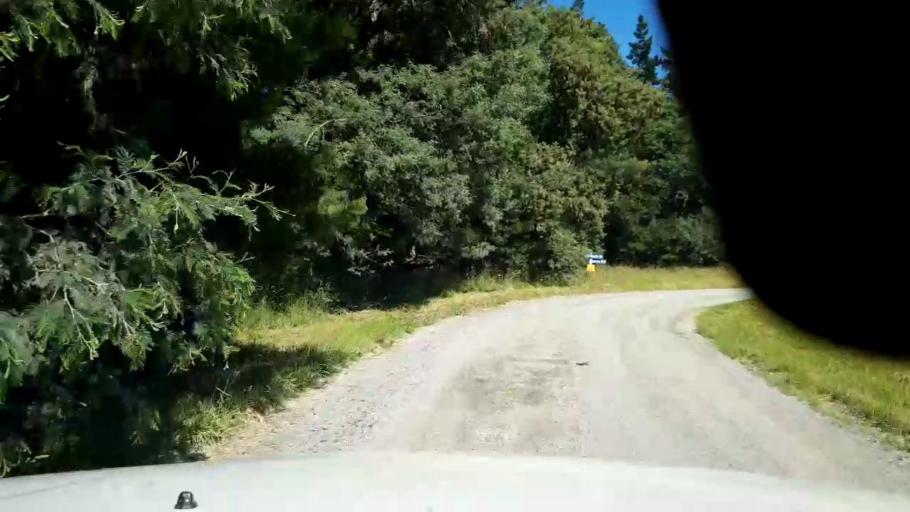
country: NZ
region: Canterbury
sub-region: Timaru District
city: Pleasant Point
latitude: -43.9677
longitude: 171.2266
